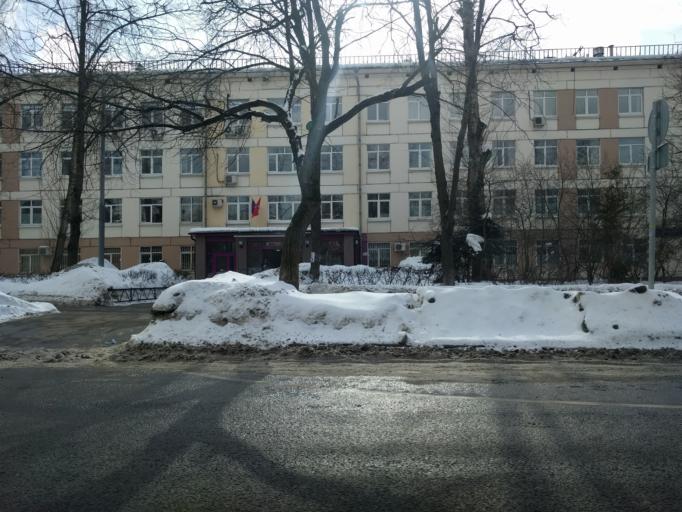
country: RU
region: Moscow
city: Metrogorodok
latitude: 55.8024
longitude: 37.7786
